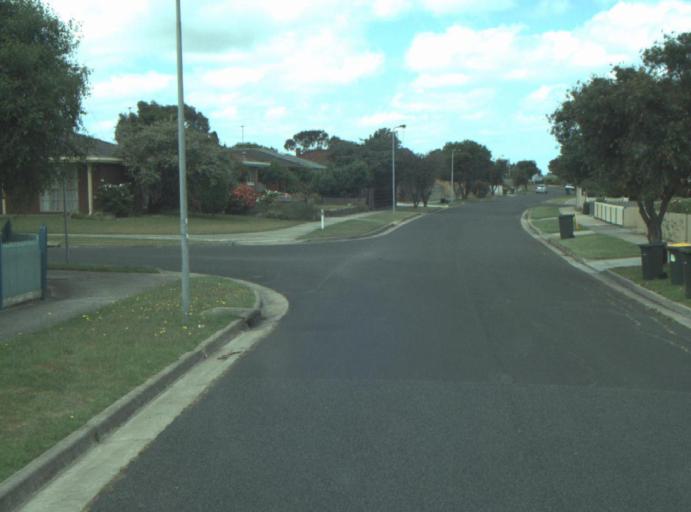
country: AU
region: Victoria
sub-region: Greater Geelong
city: Wandana Heights
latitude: -38.2118
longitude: 144.3225
